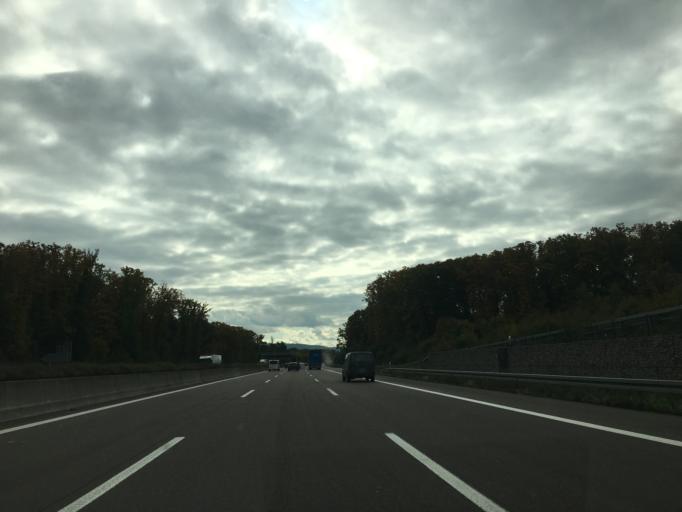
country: DE
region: Baden-Wuerttemberg
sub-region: Freiburg Region
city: Schutterwald
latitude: 48.4712
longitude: 7.9042
